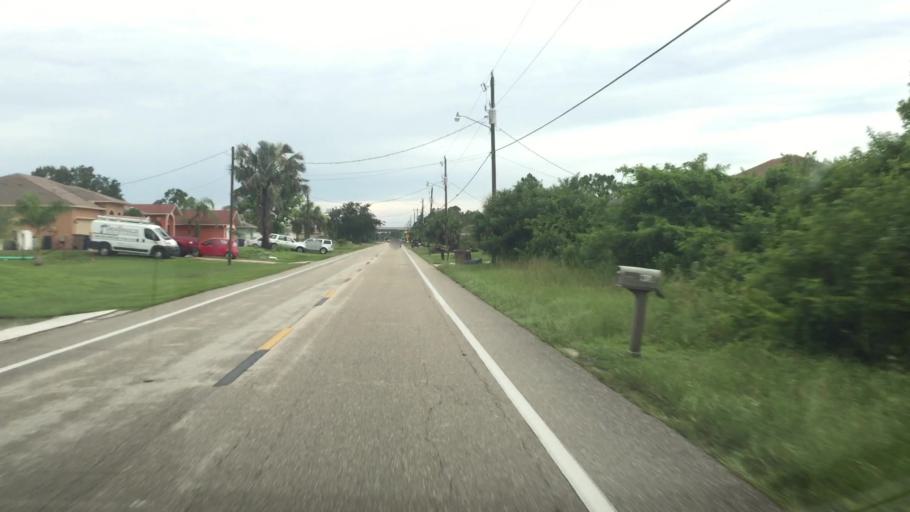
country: US
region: Florida
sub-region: Lee County
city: Gateway
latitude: 26.6268
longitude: -81.7504
